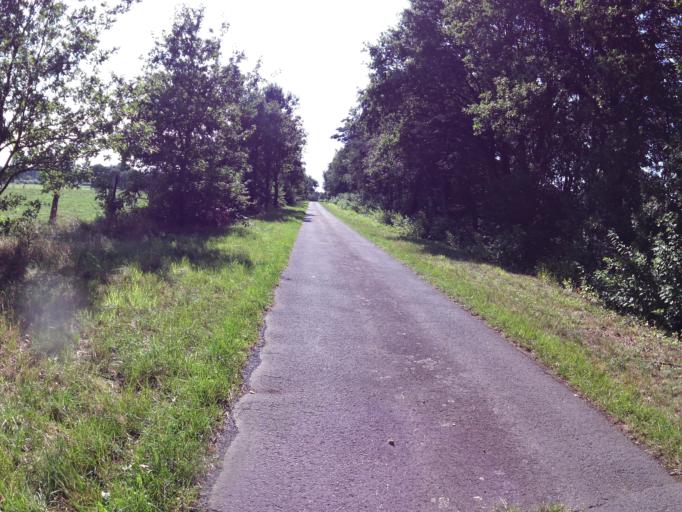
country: DE
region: Lower Saxony
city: Sandbostel
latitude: 53.3902
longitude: 9.1216
